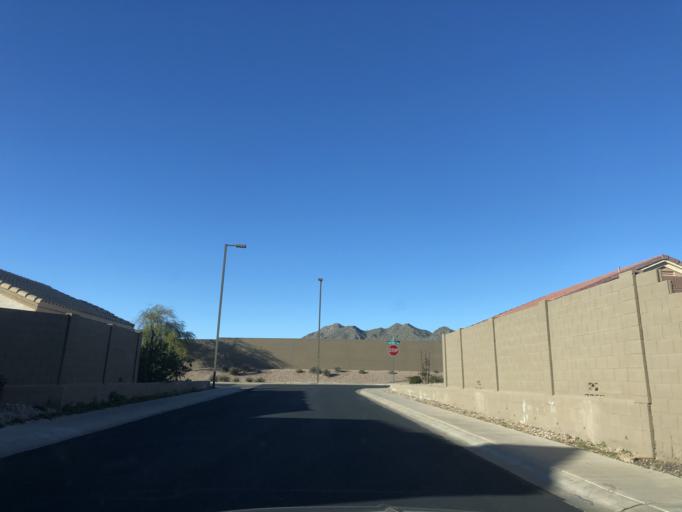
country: US
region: Arizona
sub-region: Maricopa County
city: Buckeye
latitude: 33.4395
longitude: -112.5693
